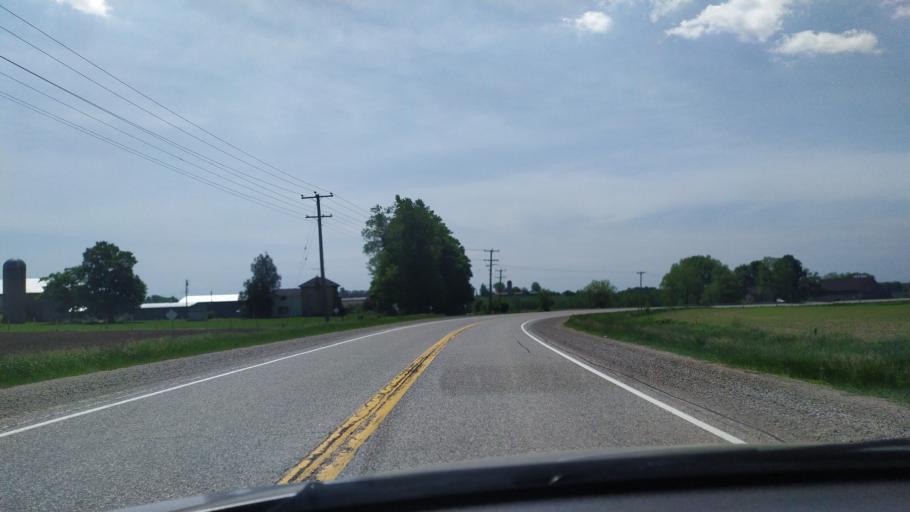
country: CA
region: Ontario
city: Dorchester
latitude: 43.0810
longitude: -81.0004
